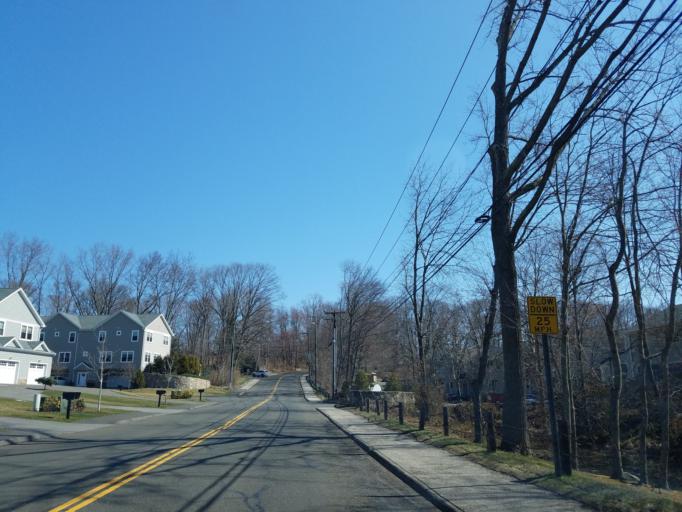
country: US
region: Connecticut
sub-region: Fairfield County
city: Norwalk
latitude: 41.1336
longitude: -73.4204
